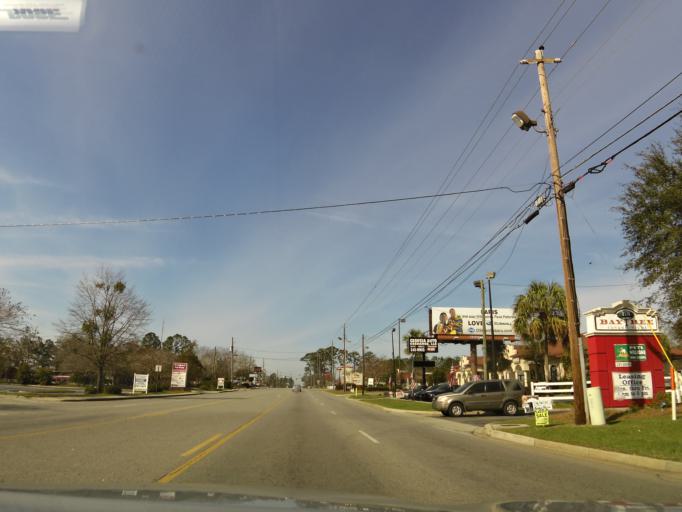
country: US
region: Georgia
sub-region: Lowndes County
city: Remerton
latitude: 30.8470
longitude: -83.3213
